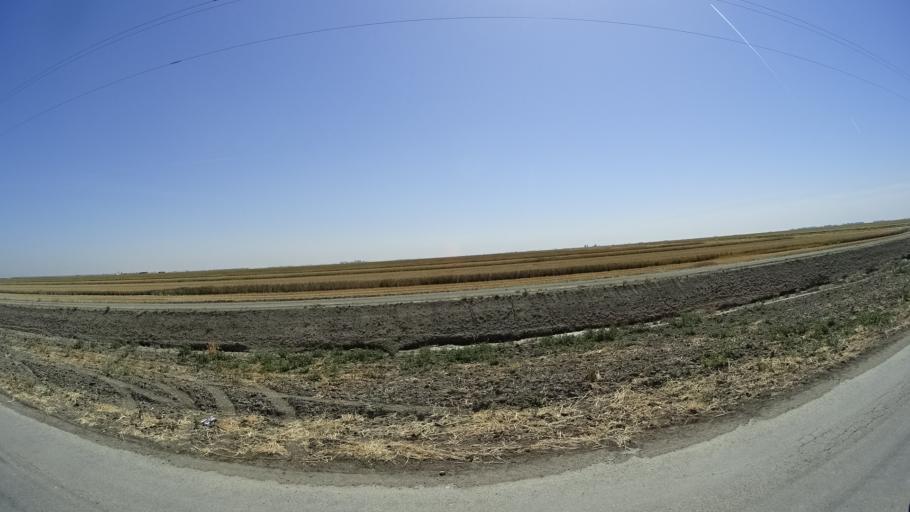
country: US
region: California
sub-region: Tulare County
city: Alpaugh
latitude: 35.9792
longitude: -119.5362
